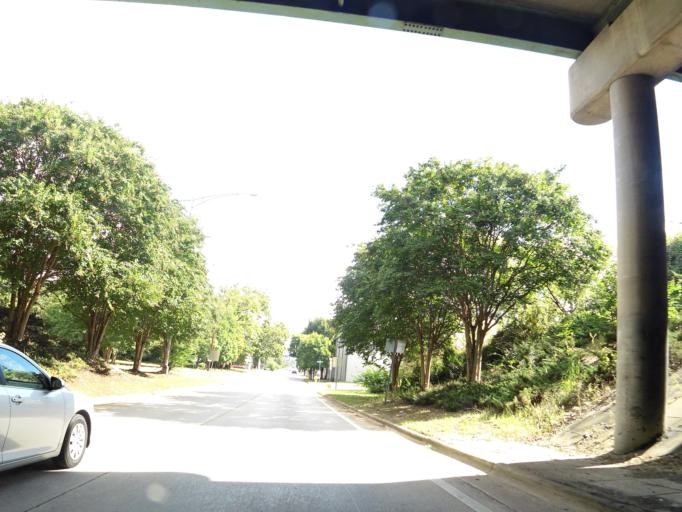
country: US
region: Alabama
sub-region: Jefferson County
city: Birmingham
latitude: 33.5026
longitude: -86.8151
